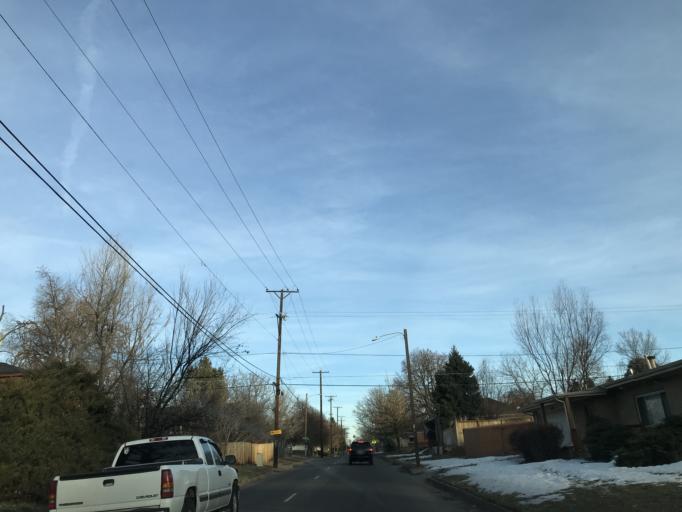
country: US
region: Colorado
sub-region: Arapahoe County
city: Glendale
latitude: 39.7387
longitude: -104.9105
